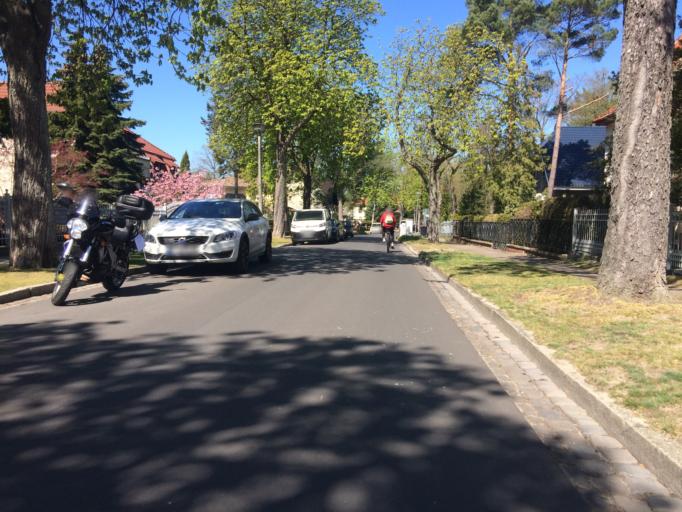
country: DE
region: Brandenburg
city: Erkner
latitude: 52.4232
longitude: 13.7192
